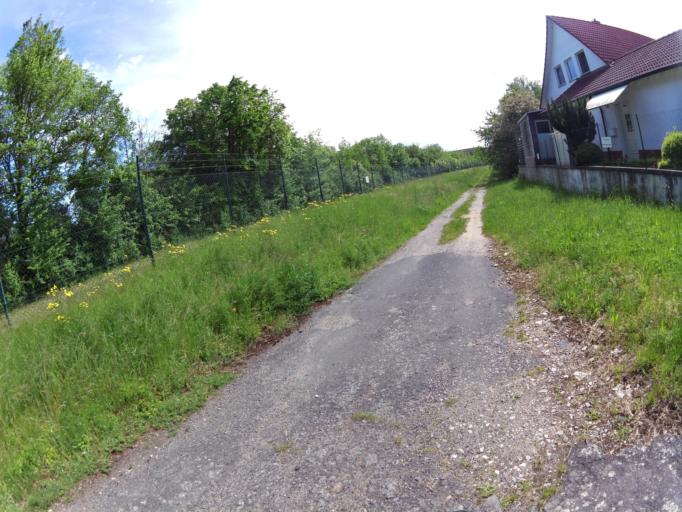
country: DE
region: Bavaria
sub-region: Regierungsbezirk Unterfranken
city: Nordheim
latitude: 49.8613
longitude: 10.1901
